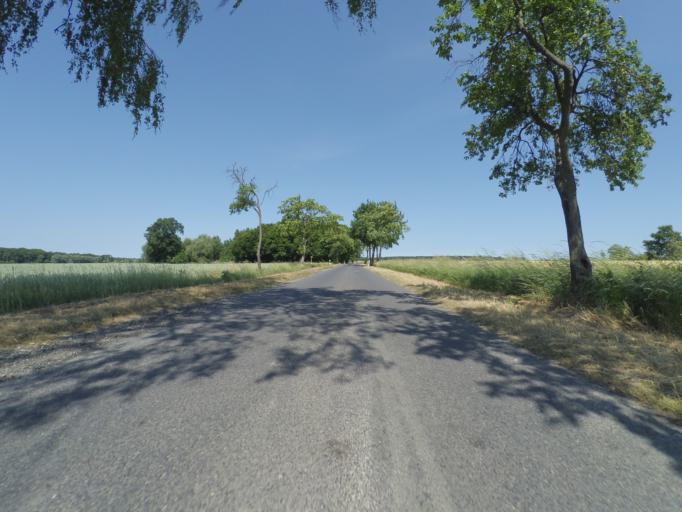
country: DE
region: Brandenburg
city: Gerdshagen
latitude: 53.2938
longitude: 12.2725
